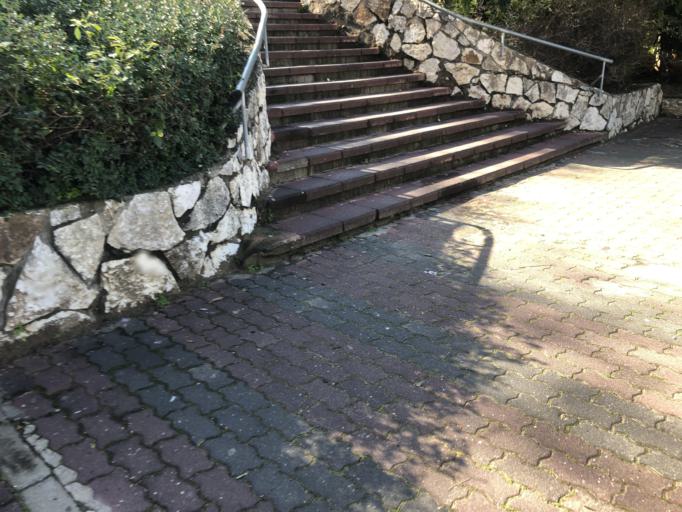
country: PS
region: West Bank
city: Az Zawiyah
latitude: 32.1097
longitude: 35.0352
